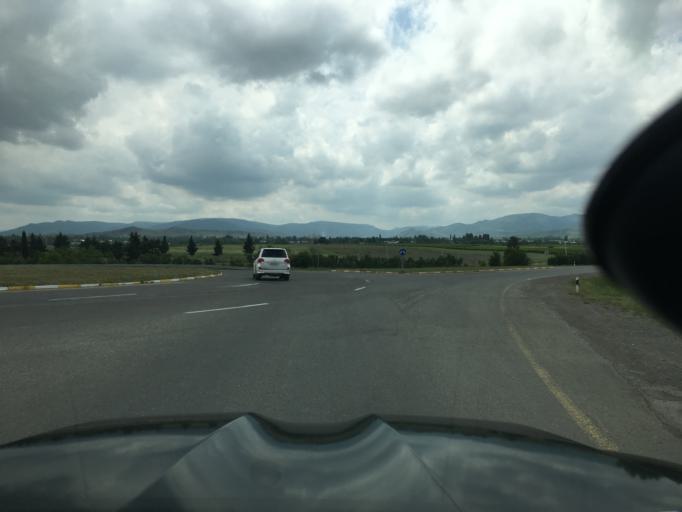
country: AZ
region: Tovuz
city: Tovuz
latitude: 40.9791
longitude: 45.6681
